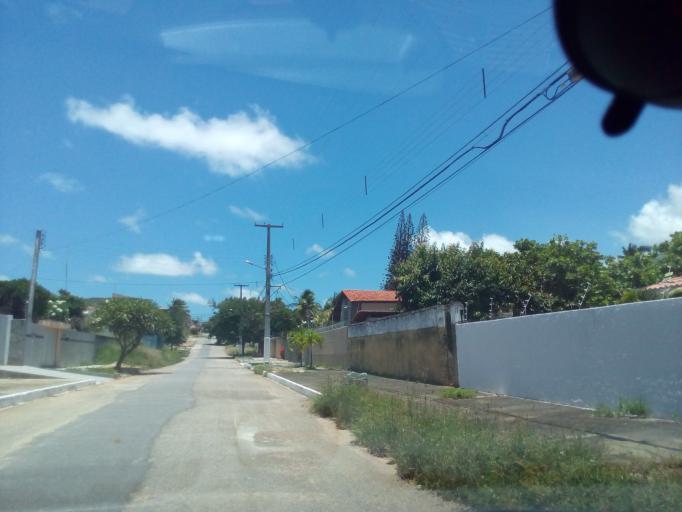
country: BR
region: Rio Grande do Norte
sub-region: Natal
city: Natal
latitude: -5.8458
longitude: -35.2074
